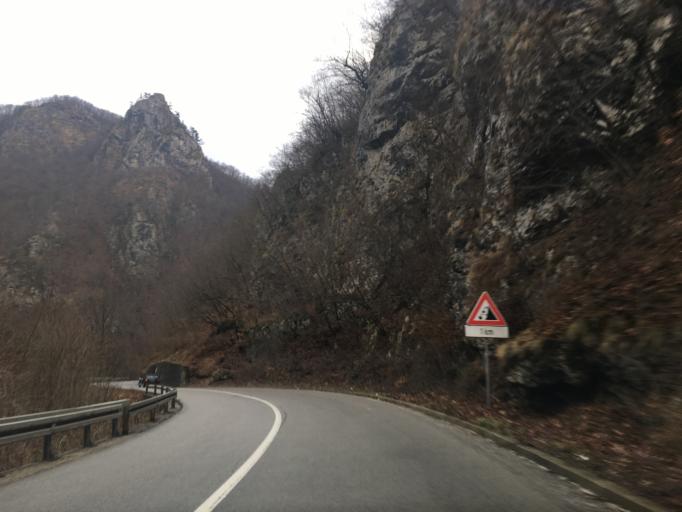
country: RS
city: Sokolovo Brdo
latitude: 43.1729
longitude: 19.7725
